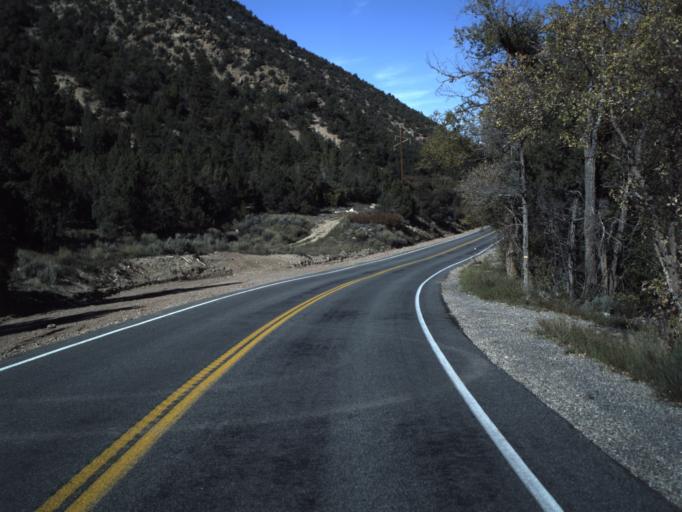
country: US
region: Utah
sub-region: Iron County
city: Parowan
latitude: 37.7753
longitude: -112.8386
